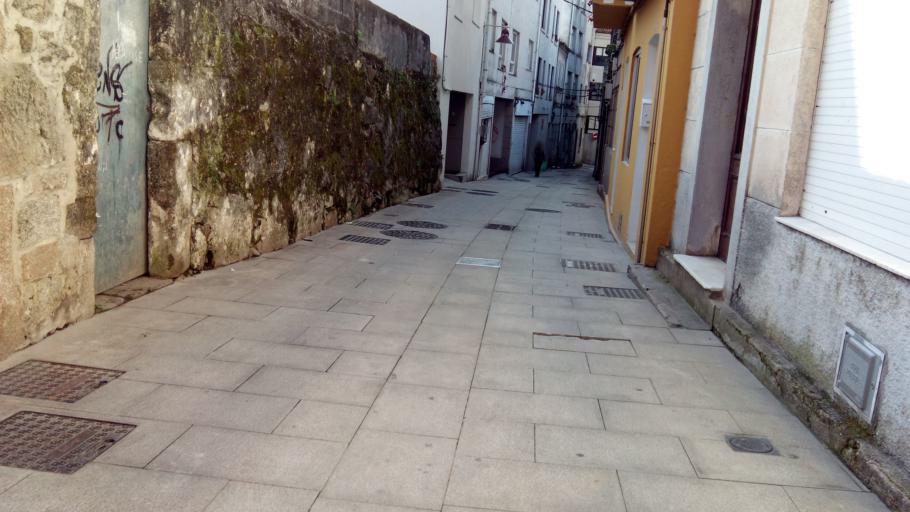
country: ES
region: Galicia
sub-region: Provincia de Pontevedra
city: Marin
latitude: 42.3918
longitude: -8.7036
